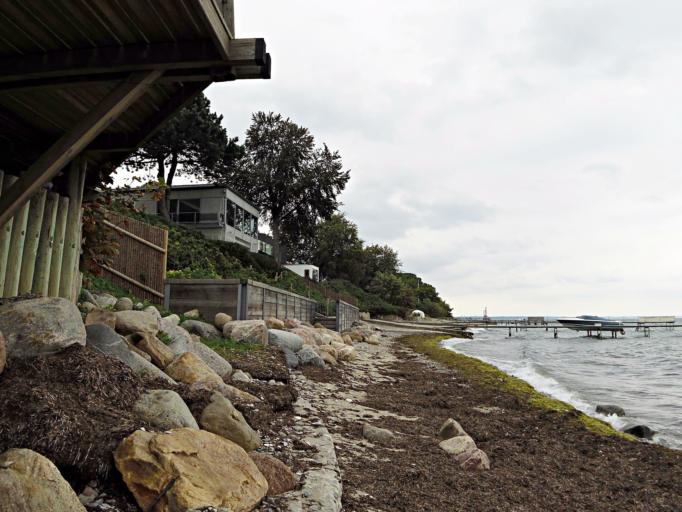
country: DK
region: Capital Region
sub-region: Rudersdal Kommune
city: Trorod
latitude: 55.8642
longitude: 12.5609
